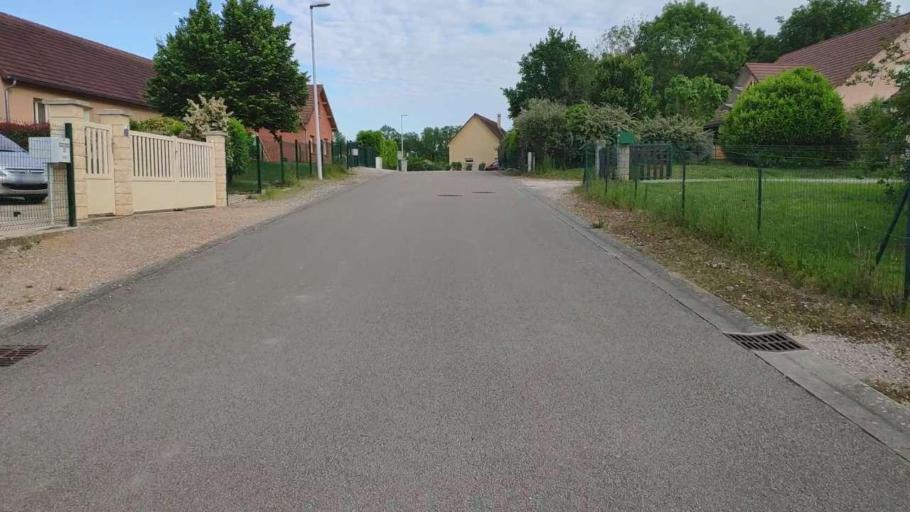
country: FR
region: Franche-Comte
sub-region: Departement du Jura
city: Bletterans
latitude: 46.7508
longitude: 5.4465
